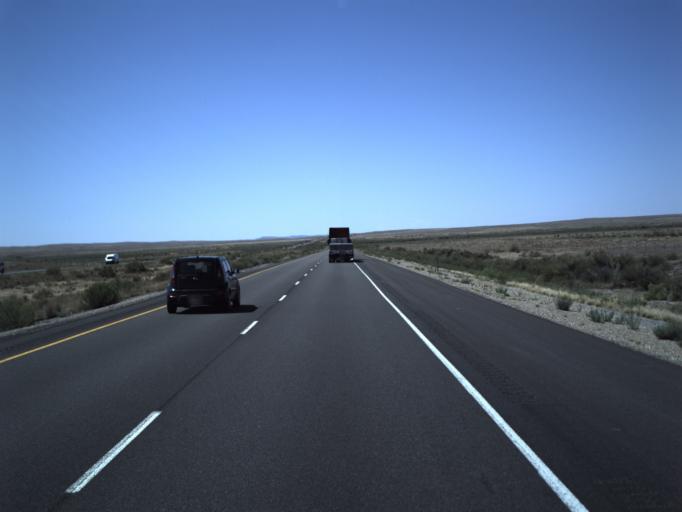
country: US
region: Colorado
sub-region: Mesa County
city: Loma
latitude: 39.0884
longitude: -109.2170
